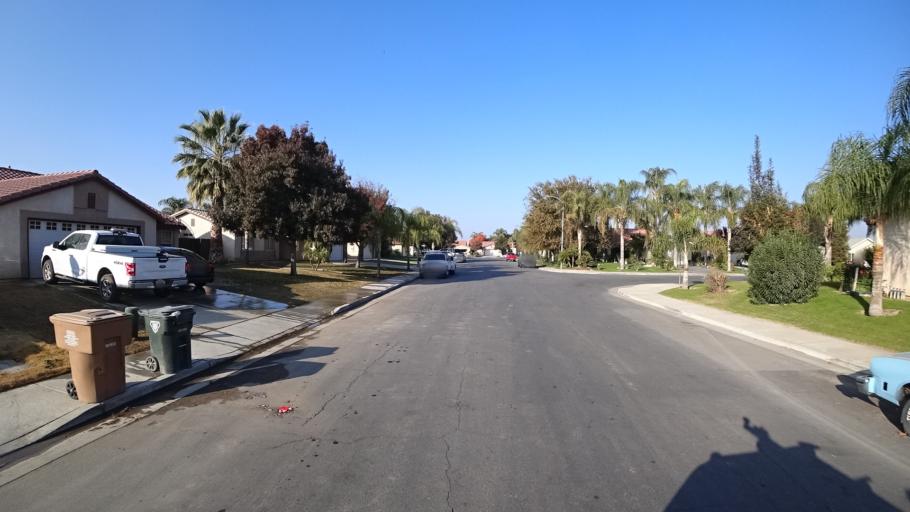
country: US
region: California
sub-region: Kern County
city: Greenfield
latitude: 35.2860
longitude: -119.0137
